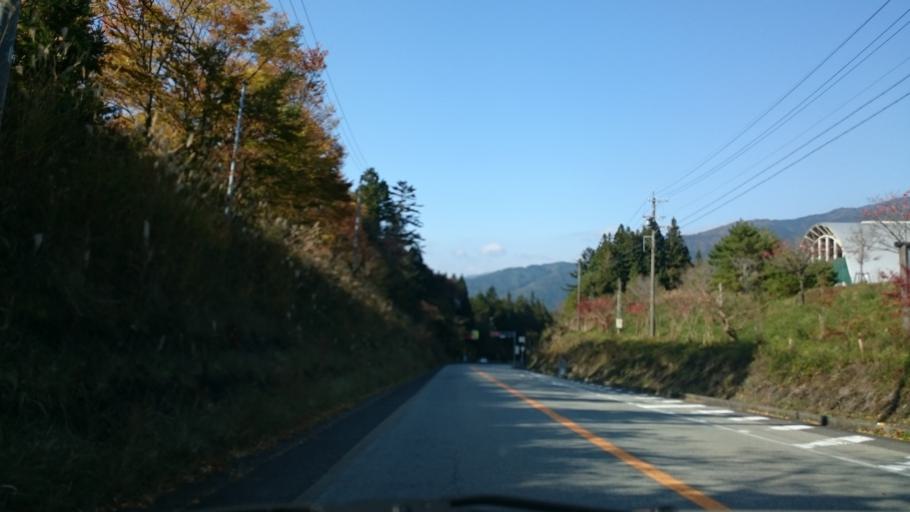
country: JP
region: Gifu
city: Nakatsugawa
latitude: 35.7506
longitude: 137.3287
